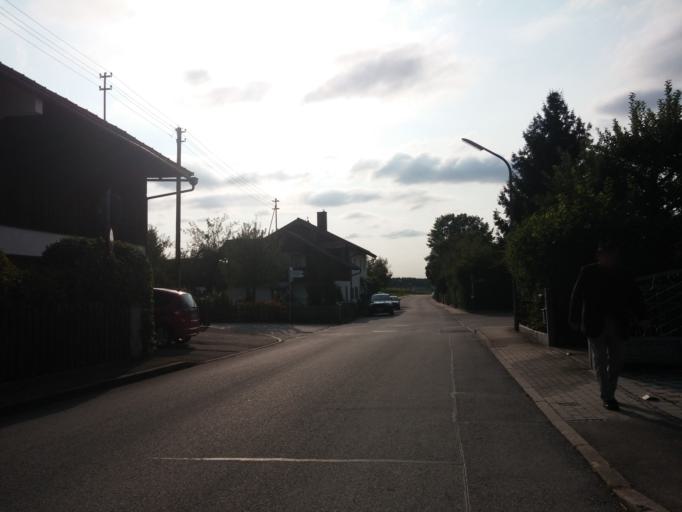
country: DE
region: Bavaria
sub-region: Upper Bavaria
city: Oberpframmern
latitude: 48.0214
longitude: 11.8106
